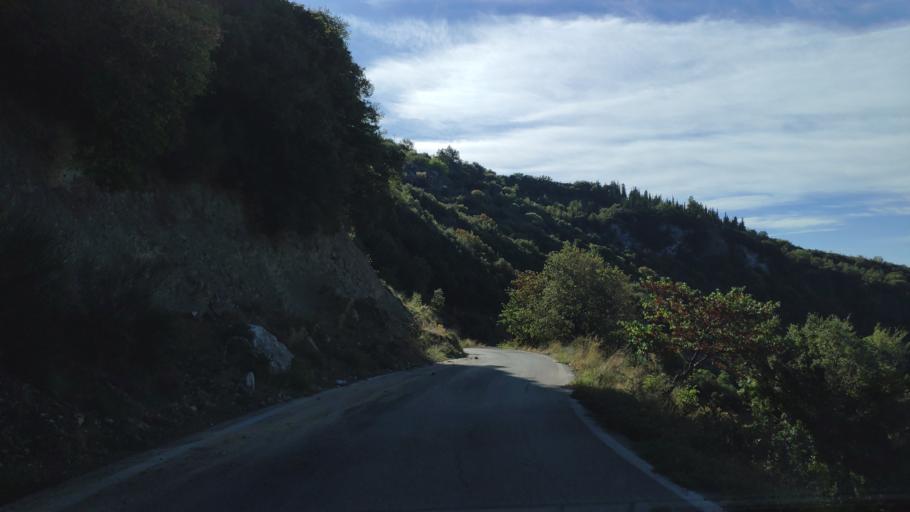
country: GR
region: Peloponnese
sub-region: Nomos Arkadias
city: Dimitsana
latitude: 37.5517
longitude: 22.0599
